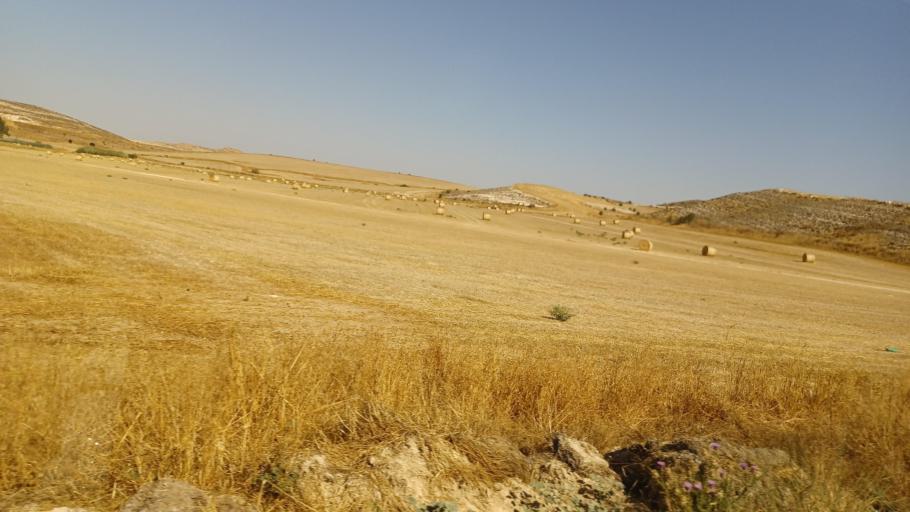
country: CY
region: Larnaka
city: Athienou
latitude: 35.0385
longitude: 33.5105
